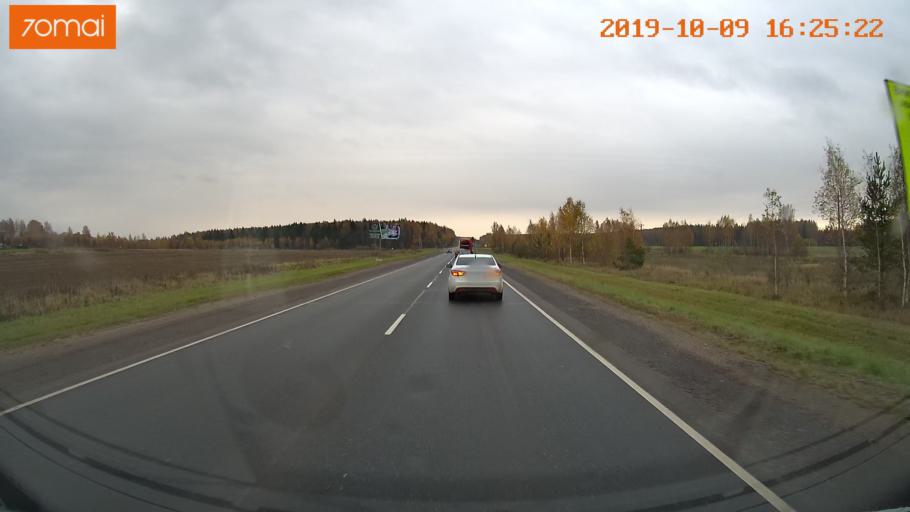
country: RU
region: Kostroma
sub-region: Kostromskoy Rayon
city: Kostroma
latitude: 57.6430
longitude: 40.9191
